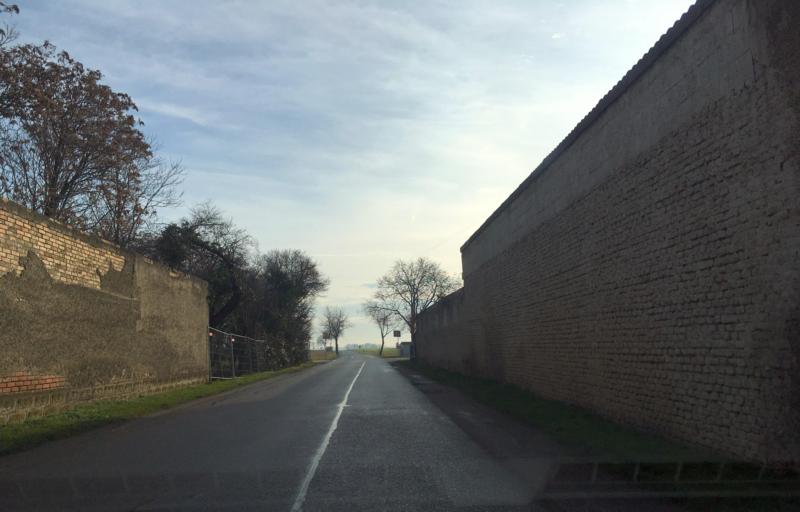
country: AT
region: Lower Austria
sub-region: Politischer Bezirk Ganserndorf
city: Leopoldsdorf im Marchfelde
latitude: 48.1946
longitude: 16.7103
